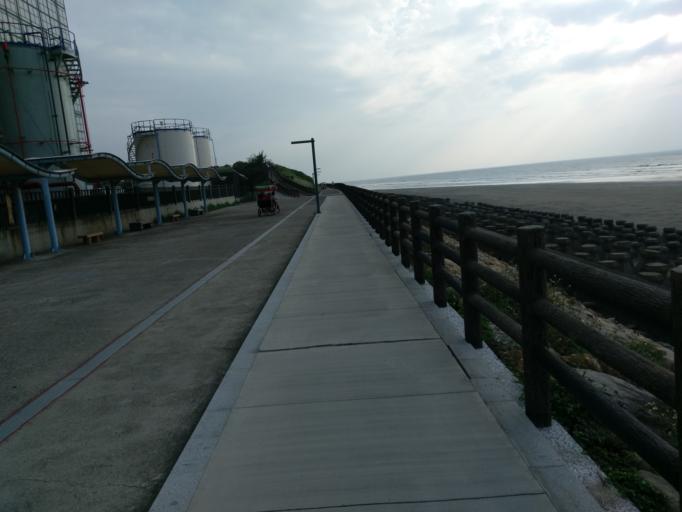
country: TW
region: Taiwan
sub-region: Hsinchu
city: Hsinchu
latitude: 24.8349
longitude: 120.9162
